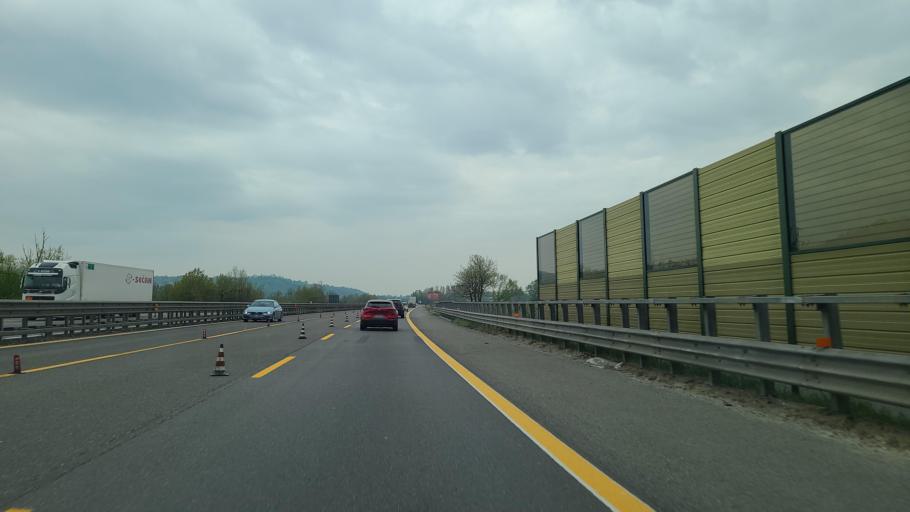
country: IT
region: Piedmont
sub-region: Provincia di Alessandria
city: Rocca Grimalda
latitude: 44.6617
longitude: 8.6590
